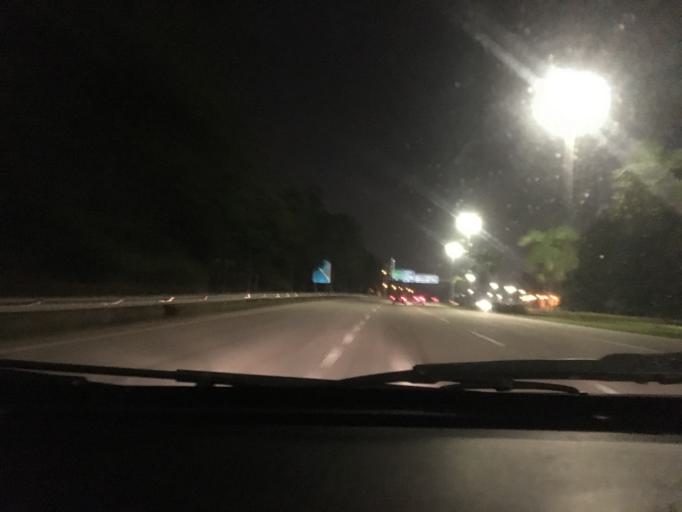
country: MY
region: Putrajaya
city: Putrajaya
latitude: 2.9200
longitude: 101.6651
